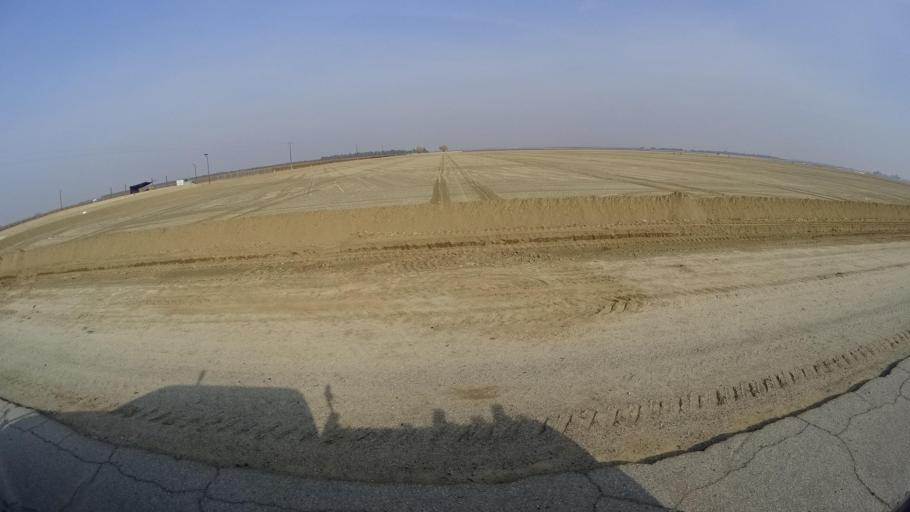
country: US
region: California
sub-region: Kern County
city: Weedpatch
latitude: 35.0933
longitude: -118.9493
